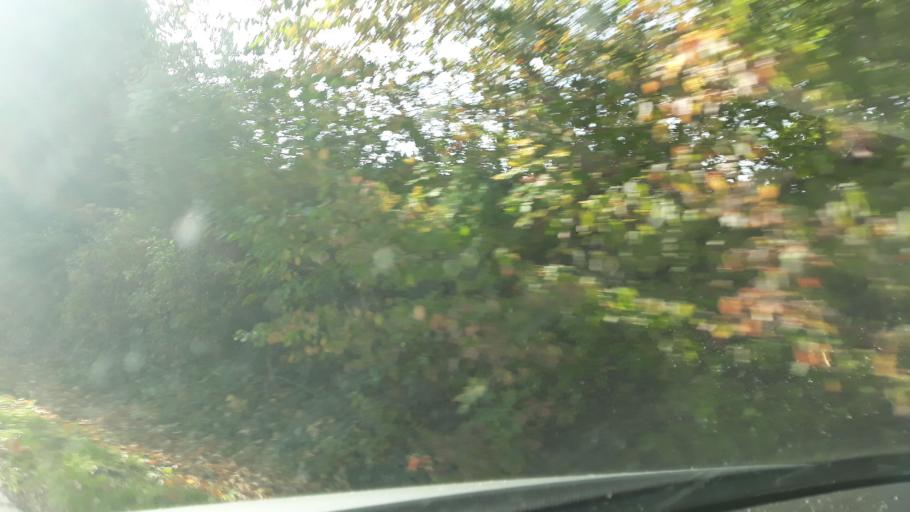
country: DE
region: Schleswig-Holstein
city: Kropp
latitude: 54.4060
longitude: 9.5108
